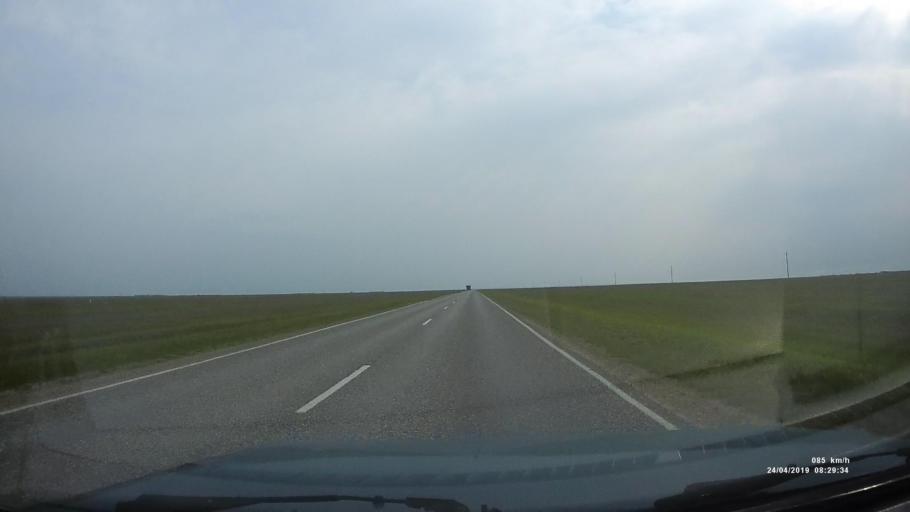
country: RU
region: Kalmykiya
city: Priyutnoye
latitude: 46.1531
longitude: 43.8328
